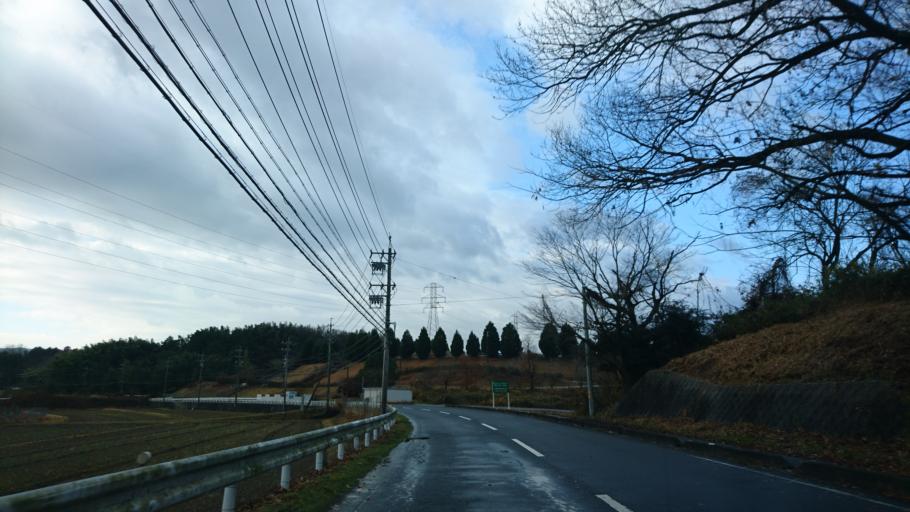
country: JP
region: Mie
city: Ueno-ebisumachi
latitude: 34.7200
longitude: 136.0779
